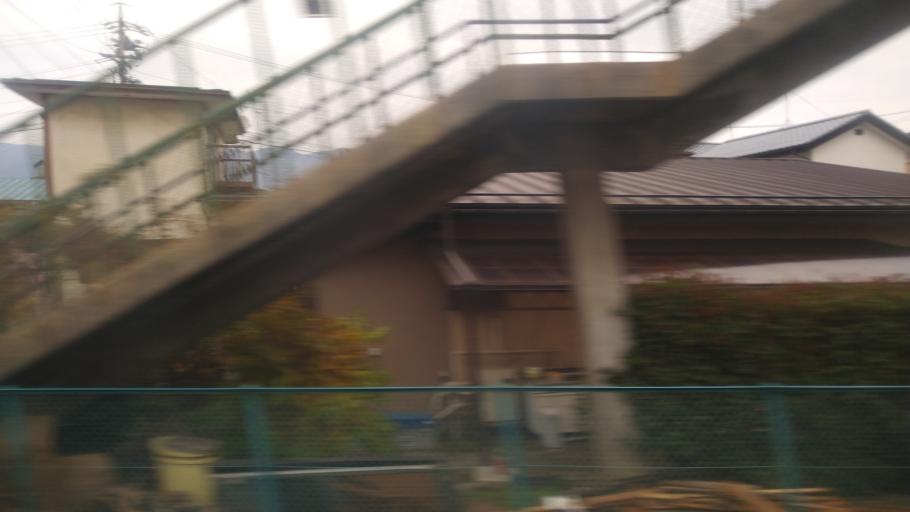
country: JP
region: Nagano
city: Matsumoto
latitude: 36.1871
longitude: 137.9609
